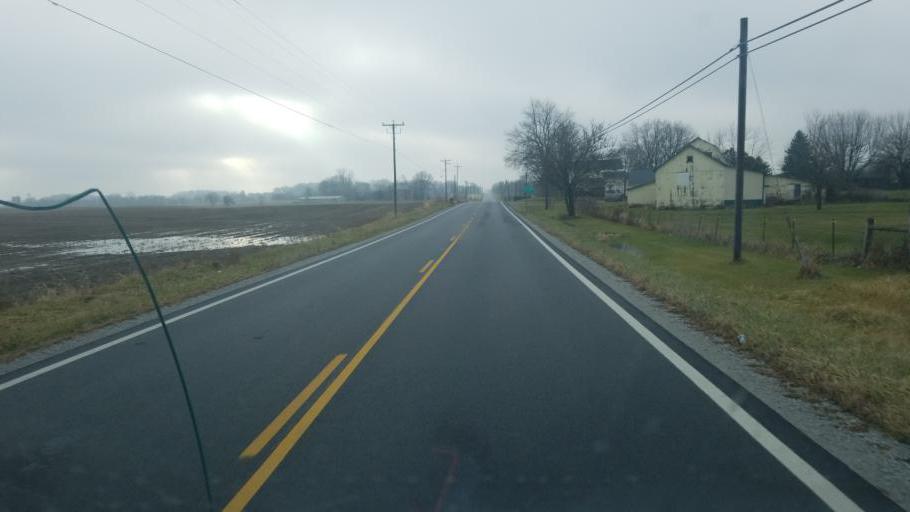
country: US
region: Ohio
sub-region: Hardin County
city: Kenton
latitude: 40.6685
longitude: -83.5459
